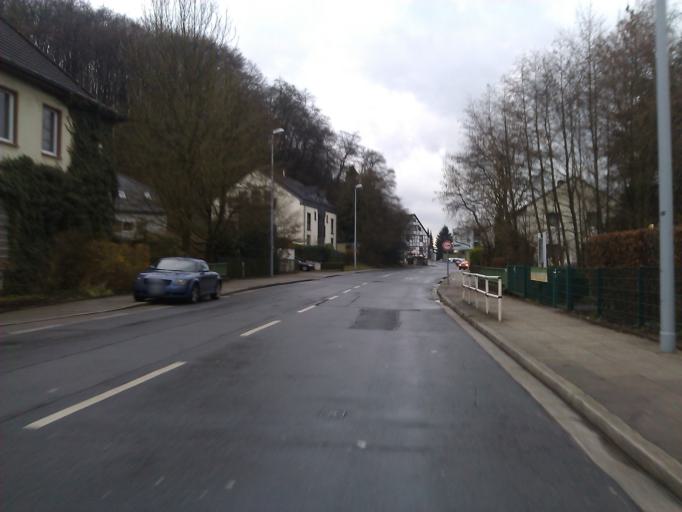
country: DE
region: North Rhine-Westphalia
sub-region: Regierungsbezirk Dusseldorf
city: Heiligenhaus
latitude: 51.3550
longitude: 6.9309
